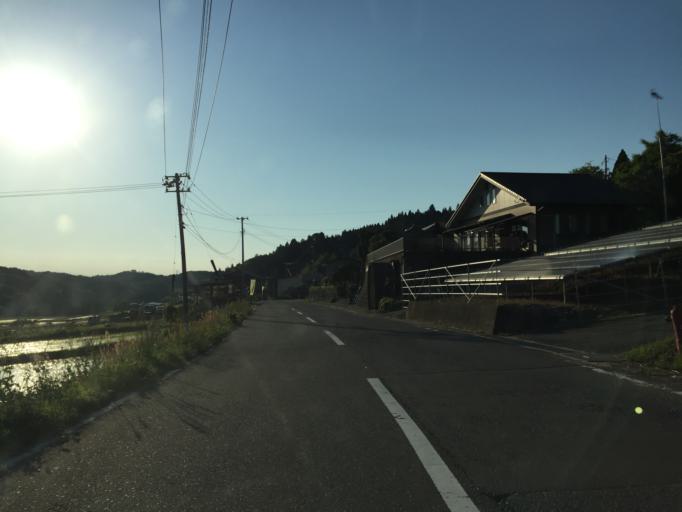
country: JP
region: Fukushima
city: Ishikawa
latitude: 37.0430
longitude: 140.4354
